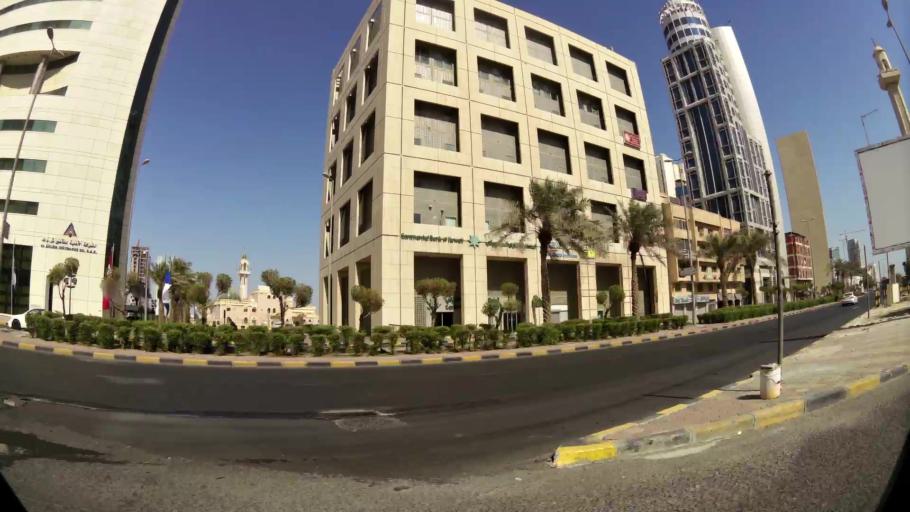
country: KW
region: Al Asimah
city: Kuwait City
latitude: 29.3824
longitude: 47.9871
